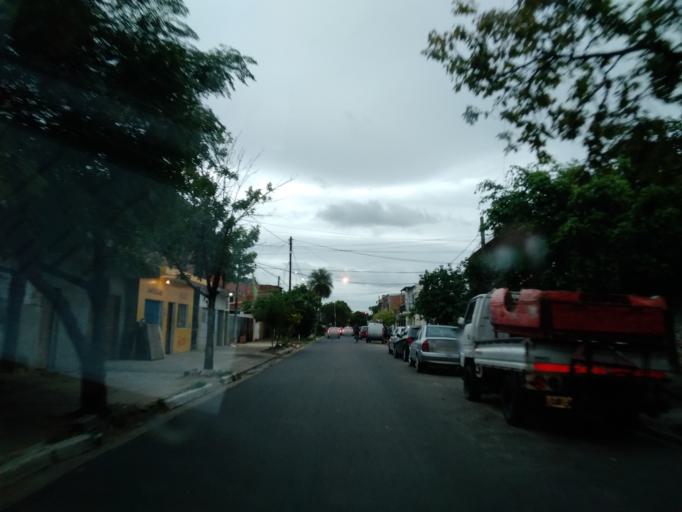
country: AR
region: Corrientes
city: Corrientes
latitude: -27.4760
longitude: -58.8249
